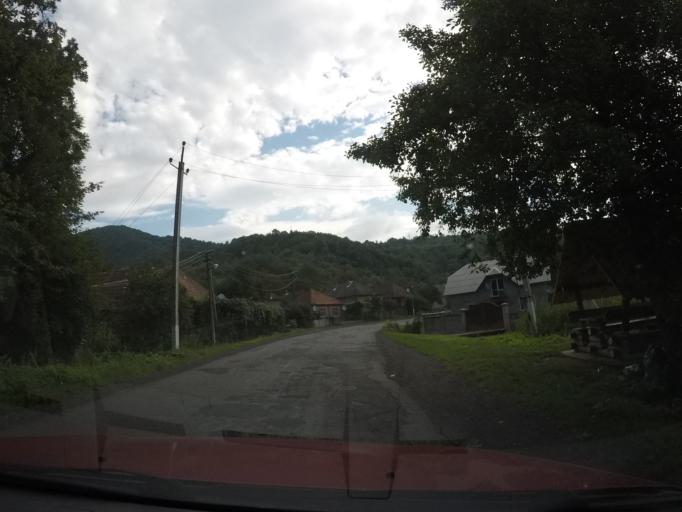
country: UA
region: Zakarpattia
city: Velykyi Bereznyi
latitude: 48.9532
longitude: 22.5266
